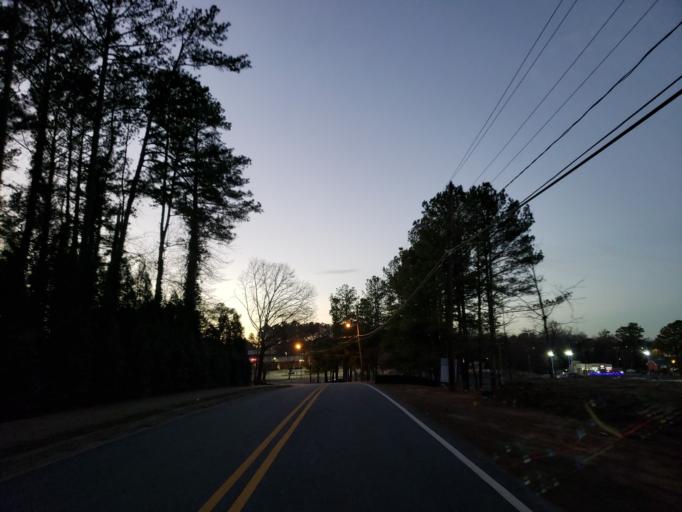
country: US
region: Georgia
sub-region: Fulton County
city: Alpharetta
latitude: 34.0677
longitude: -84.2966
